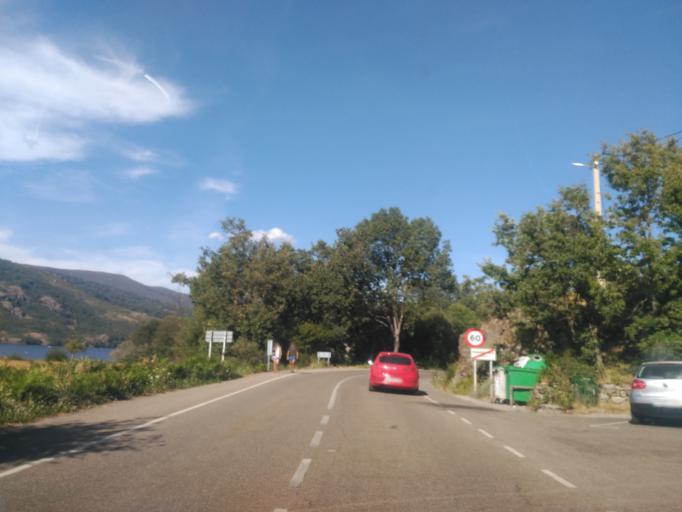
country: ES
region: Castille and Leon
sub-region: Provincia de Zamora
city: Cobreros
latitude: 42.1148
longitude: -6.7348
